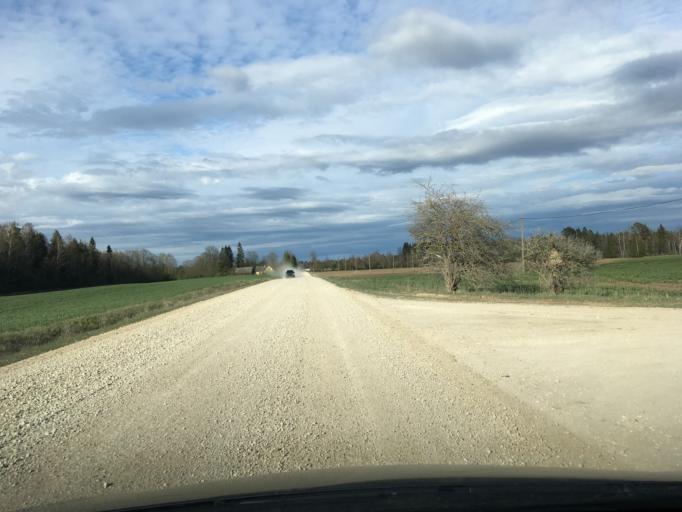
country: EE
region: Raplamaa
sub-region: Maerjamaa vald
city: Marjamaa
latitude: 58.9748
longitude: 24.3500
